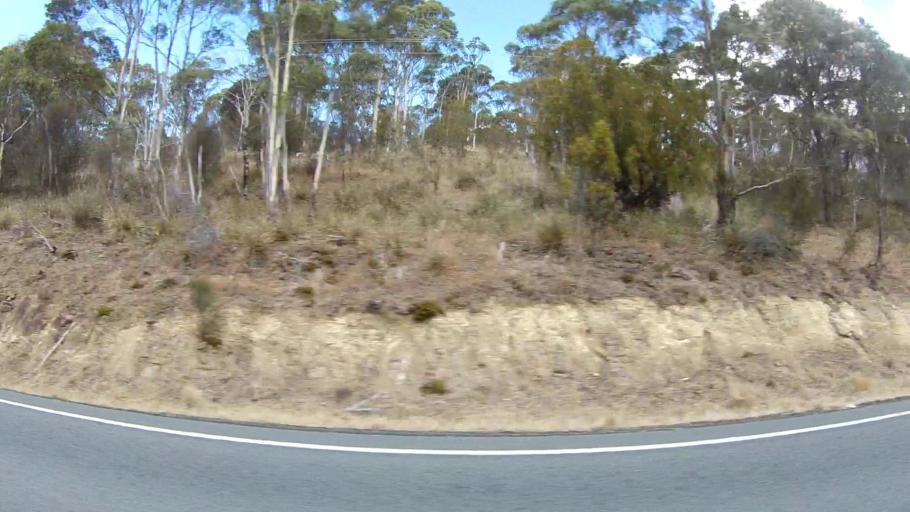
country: AU
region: Tasmania
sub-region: Sorell
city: Sorell
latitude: -42.6175
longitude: 147.6397
